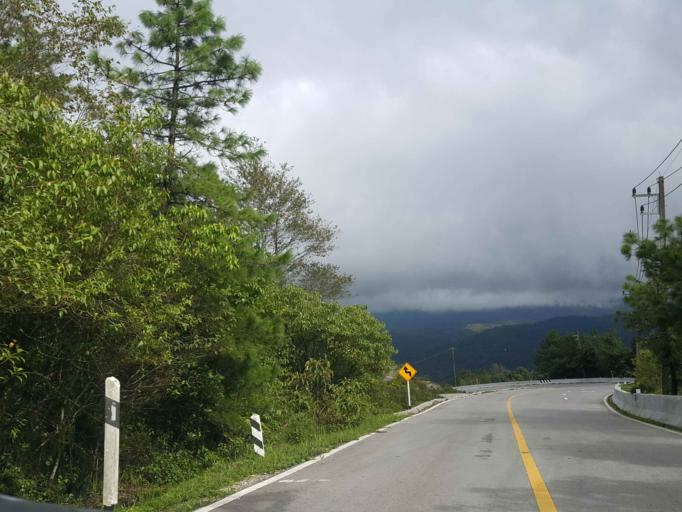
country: TH
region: Chiang Mai
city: Mae Chaem
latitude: 18.5493
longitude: 98.4826
